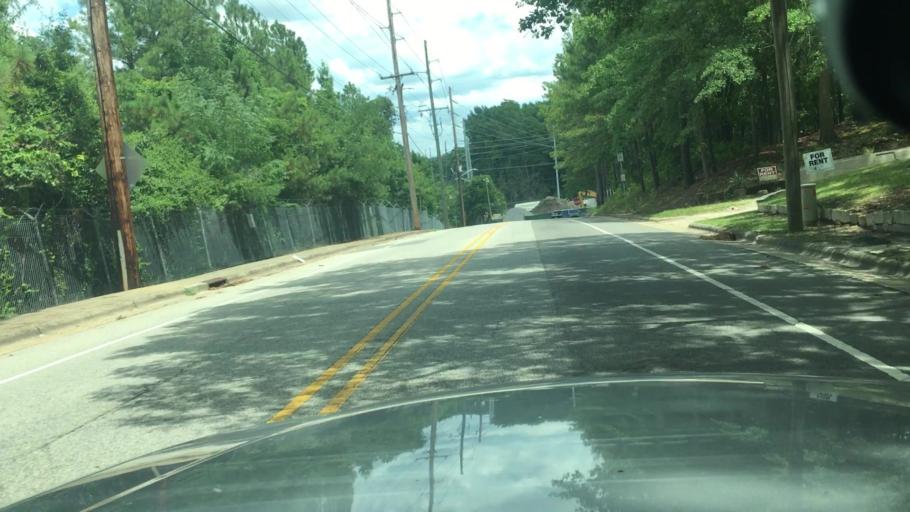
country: US
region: North Carolina
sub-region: Cumberland County
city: Fayetteville
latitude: 35.0679
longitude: -78.8974
